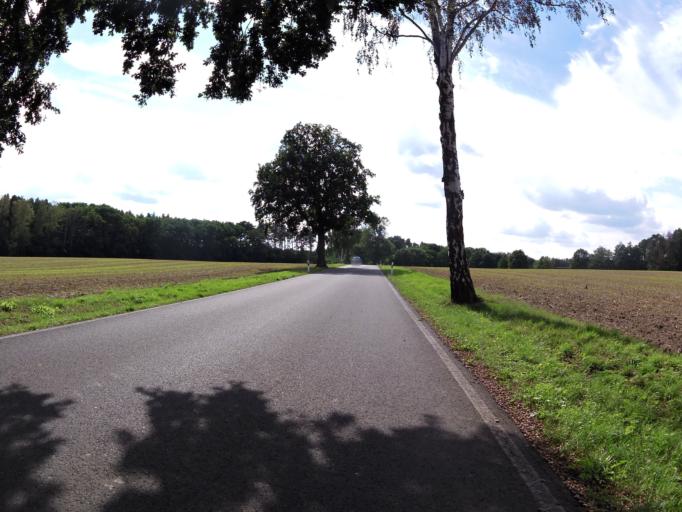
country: DE
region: Brandenburg
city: Munchehofe
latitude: 52.2053
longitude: 13.8632
